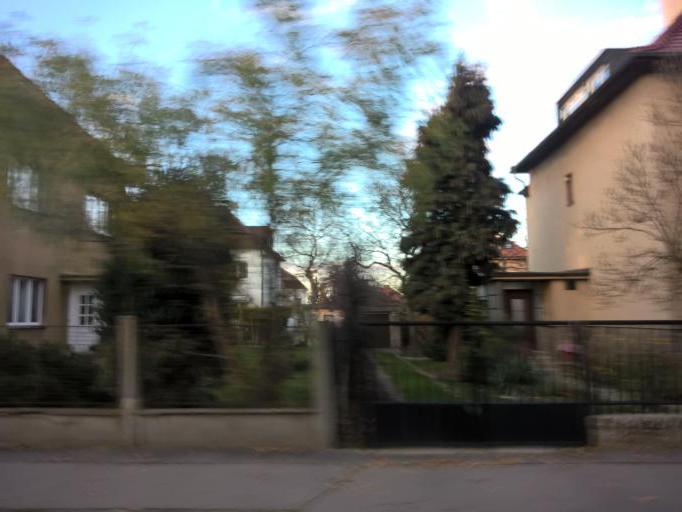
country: CZ
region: Praha
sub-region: Praha 1
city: Mala Strana
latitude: 50.0799
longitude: 14.3642
